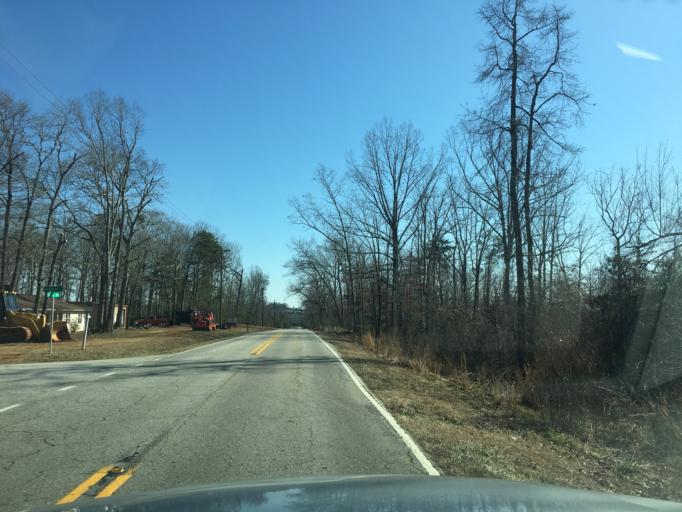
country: US
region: South Carolina
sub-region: Pickens County
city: Liberty
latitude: 34.8052
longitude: -82.7594
